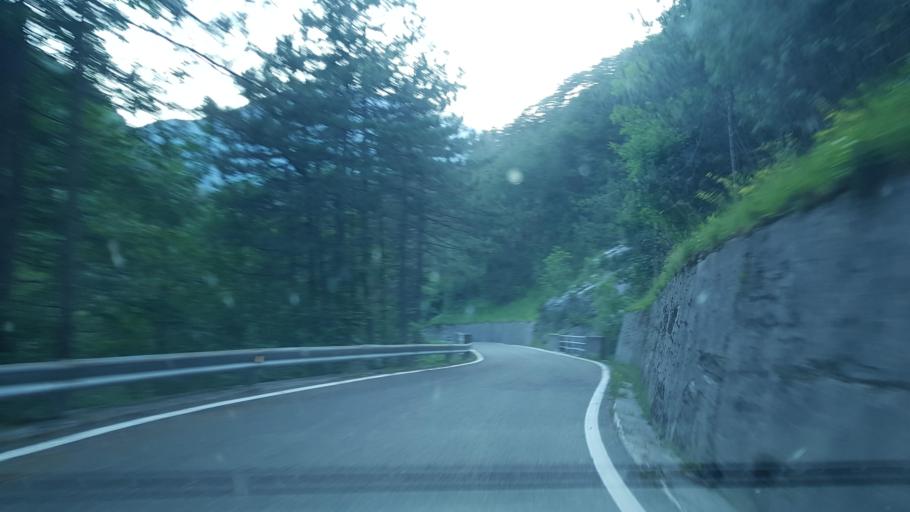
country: IT
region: Friuli Venezia Giulia
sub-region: Provincia di Udine
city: Dogna
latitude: 46.4490
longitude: 13.3431
